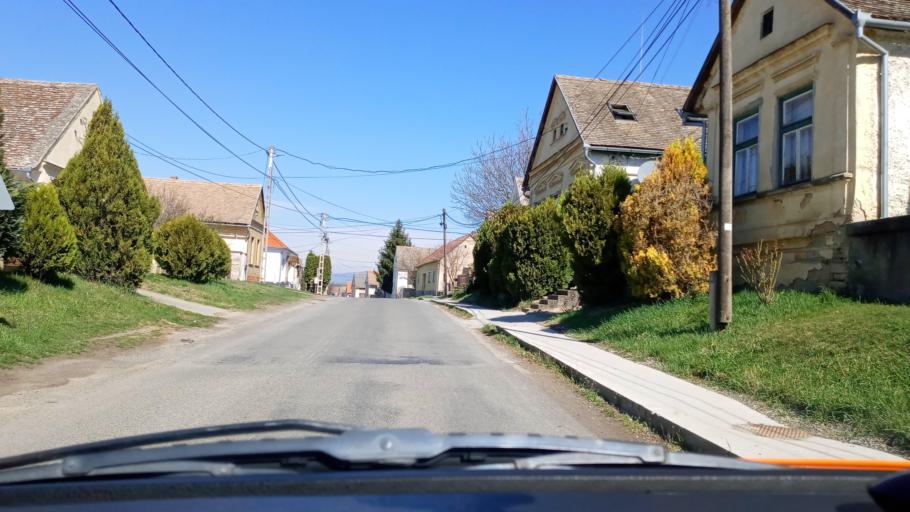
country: HU
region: Baranya
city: Boly
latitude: 46.0258
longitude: 18.4627
